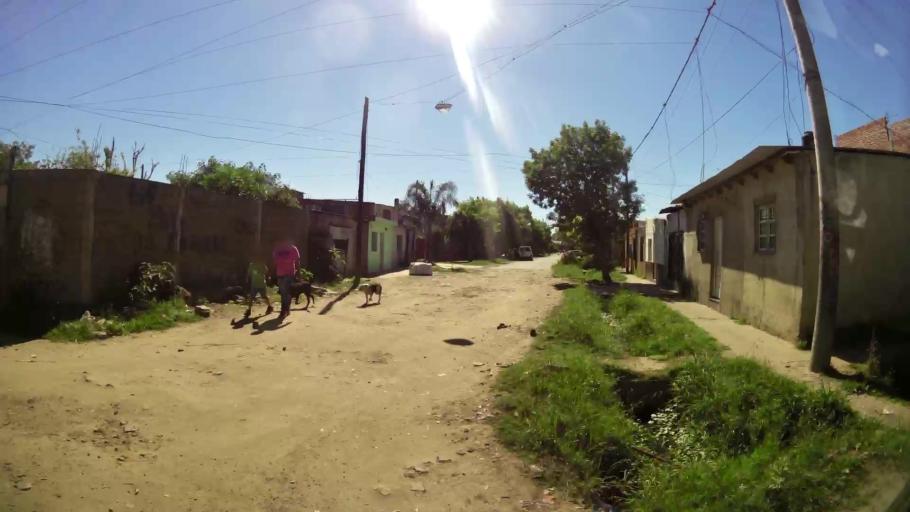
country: AR
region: Santa Fe
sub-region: Departamento de Rosario
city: Rosario
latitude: -32.9543
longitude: -60.6916
